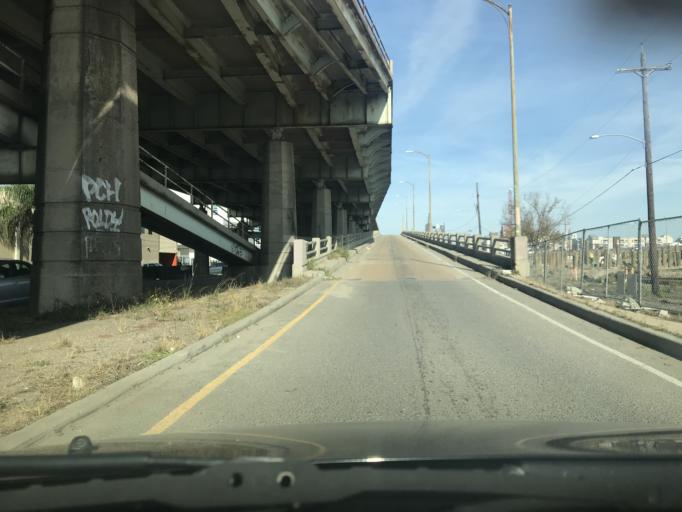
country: US
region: Louisiana
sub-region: Orleans Parish
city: New Orleans
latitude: 29.9560
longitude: -90.0954
